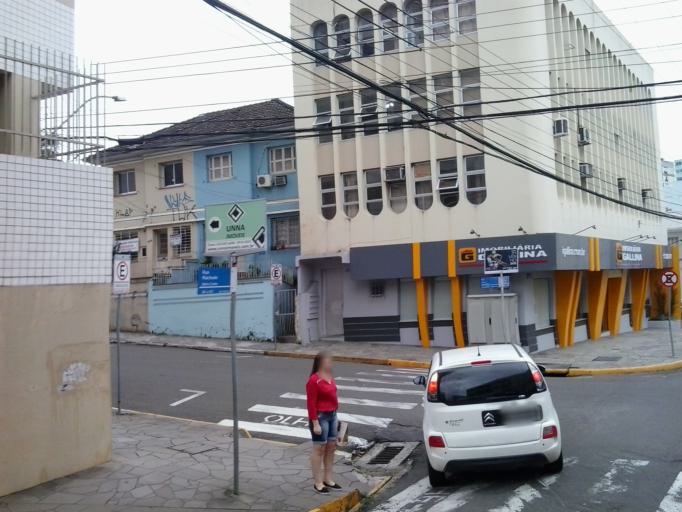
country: BR
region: Rio Grande do Sul
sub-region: Santa Maria
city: Santa Maria
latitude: -29.6878
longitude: -53.8042
